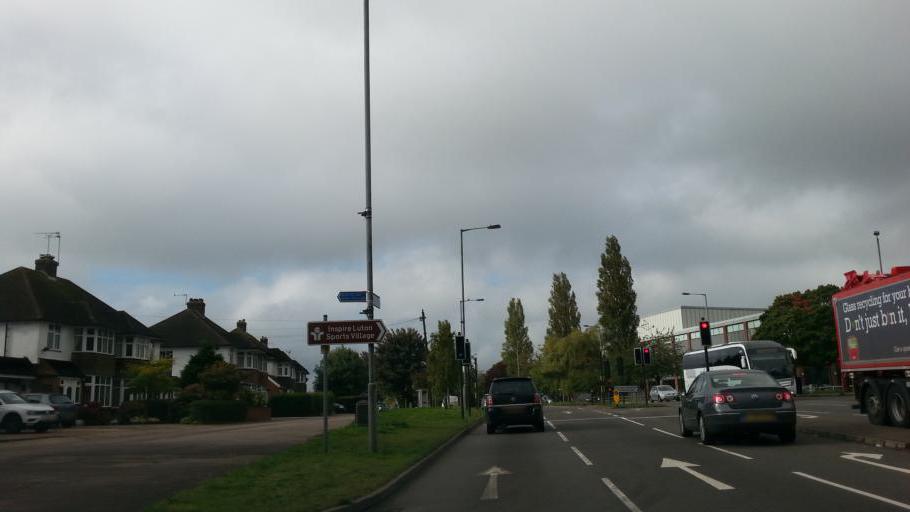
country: GB
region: England
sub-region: Luton
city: Luton
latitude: 51.9064
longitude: -0.3917
